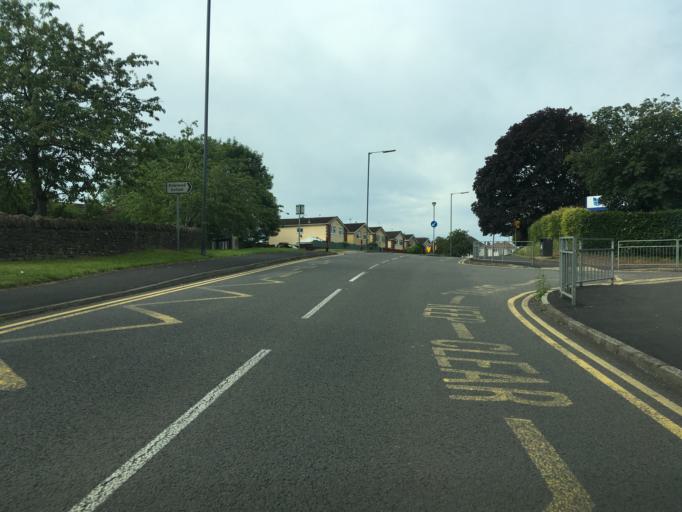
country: GB
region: England
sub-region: South Gloucestershire
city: Mangotsfield
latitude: 51.4921
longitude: -2.4926
